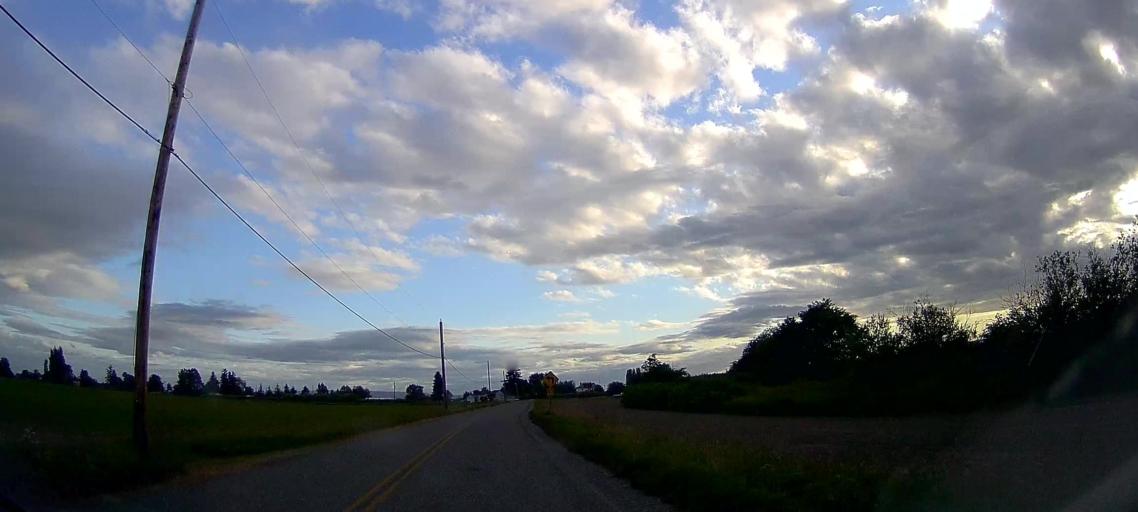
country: US
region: Washington
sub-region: Skagit County
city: Mount Vernon
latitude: 48.3469
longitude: -122.3872
